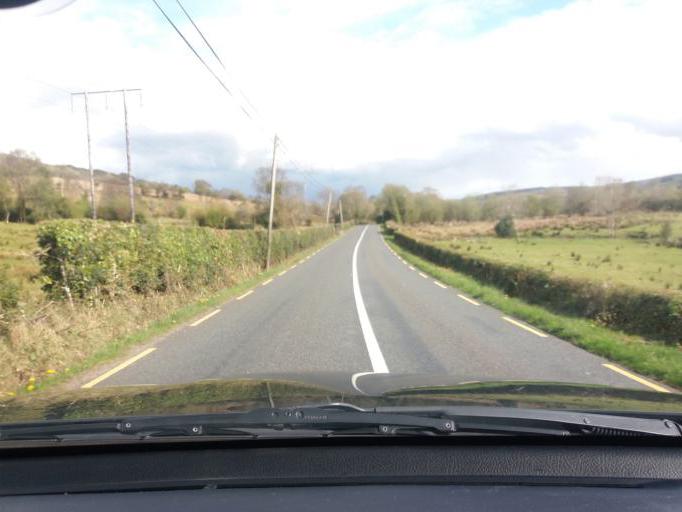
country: IE
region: Connaught
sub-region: County Leitrim
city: Kinlough
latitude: 54.3681
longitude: -8.2654
